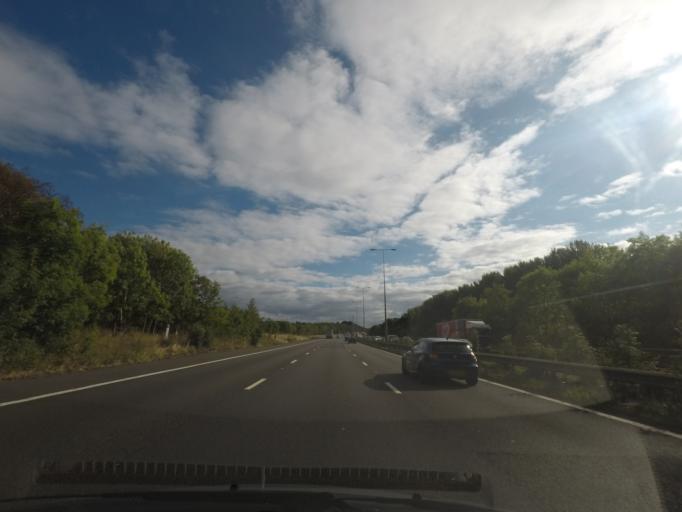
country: GB
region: England
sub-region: Leicestershire
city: Shepshed
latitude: 52.7590
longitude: -1.2737
